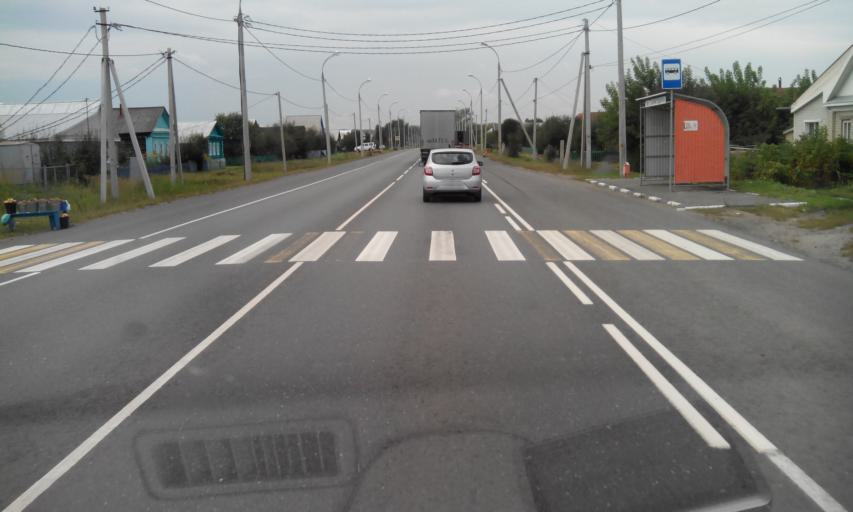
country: RU
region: Penza
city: Poselki
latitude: 53.1012
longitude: 46.4202
